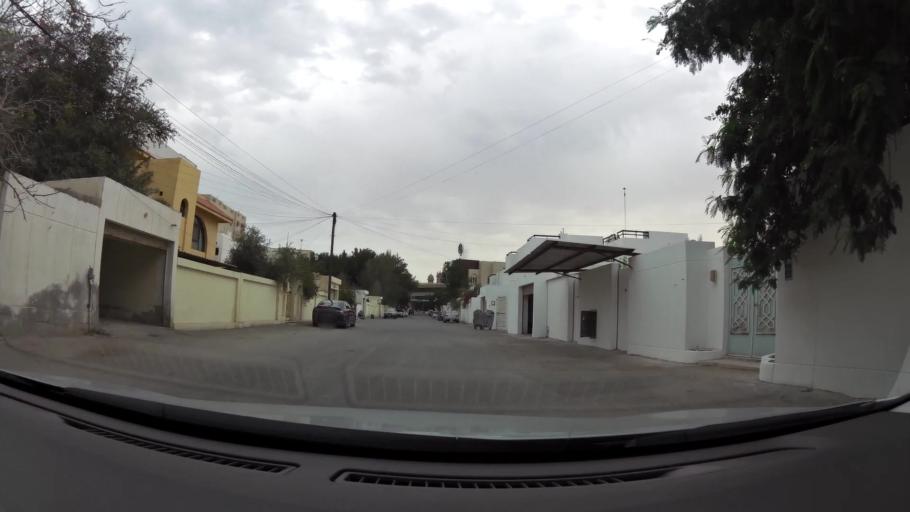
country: QA
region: Baladiyat ad Dawhah
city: Doha
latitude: 25.2758
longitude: 51.5037
